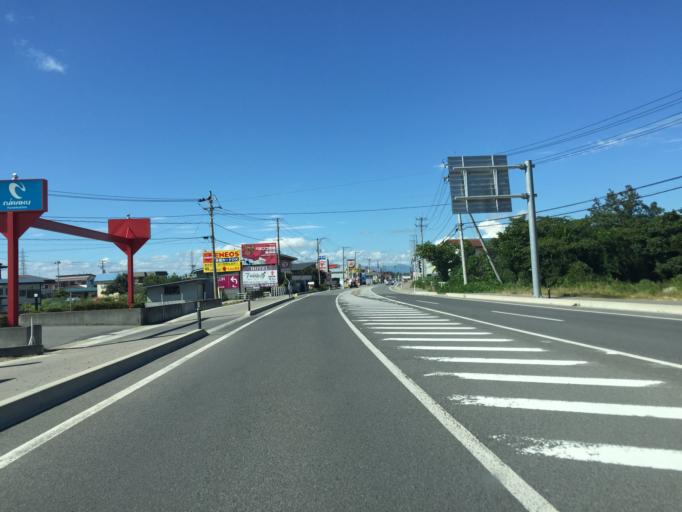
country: JP
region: Yamagata
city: Yonezawa
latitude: 37.9013
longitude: 140.1392
